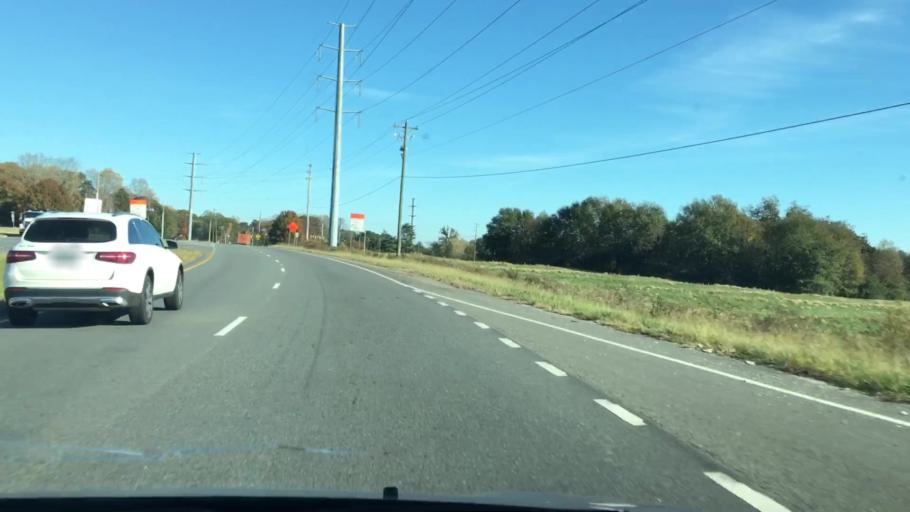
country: US
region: Georgia
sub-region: Fulton County
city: Milton
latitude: 34.1308
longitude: -84.2346
